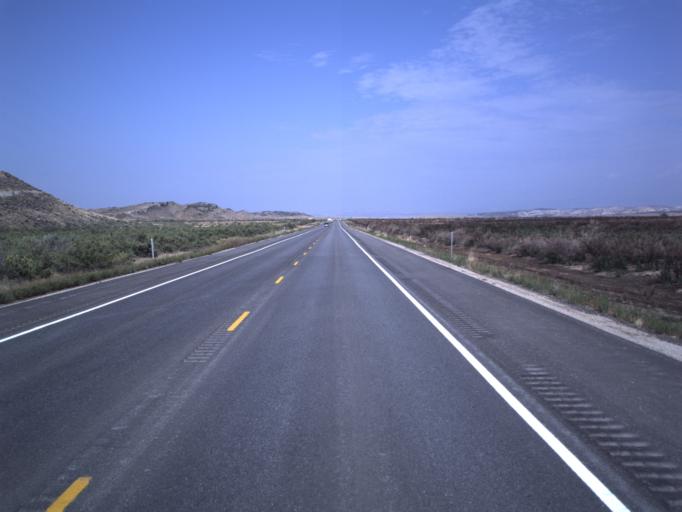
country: US
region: Utah
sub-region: Uintah County
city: Naples
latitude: 40.2885
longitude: -109.1514
